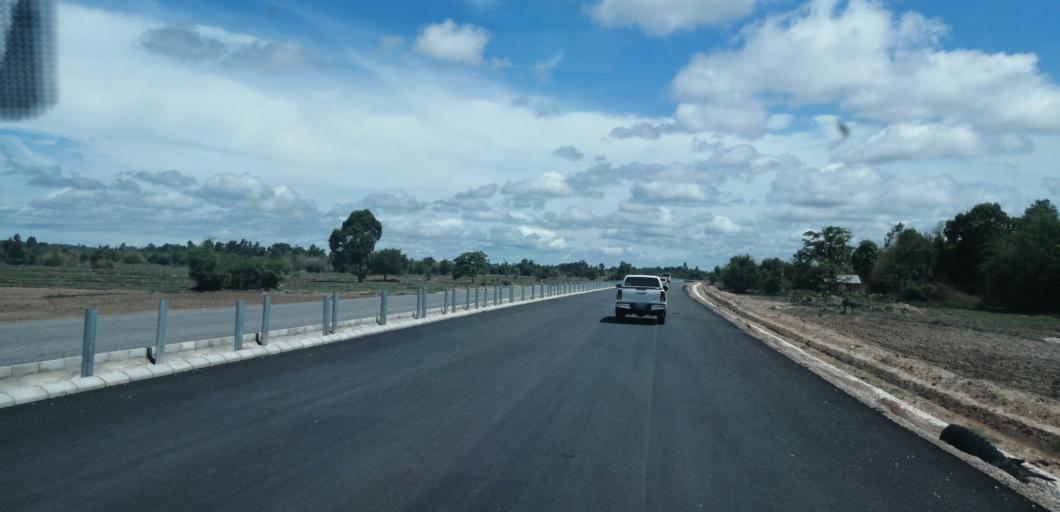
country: LA
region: Vientiane
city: Vientiane
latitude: 18.0686
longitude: 102.5162
